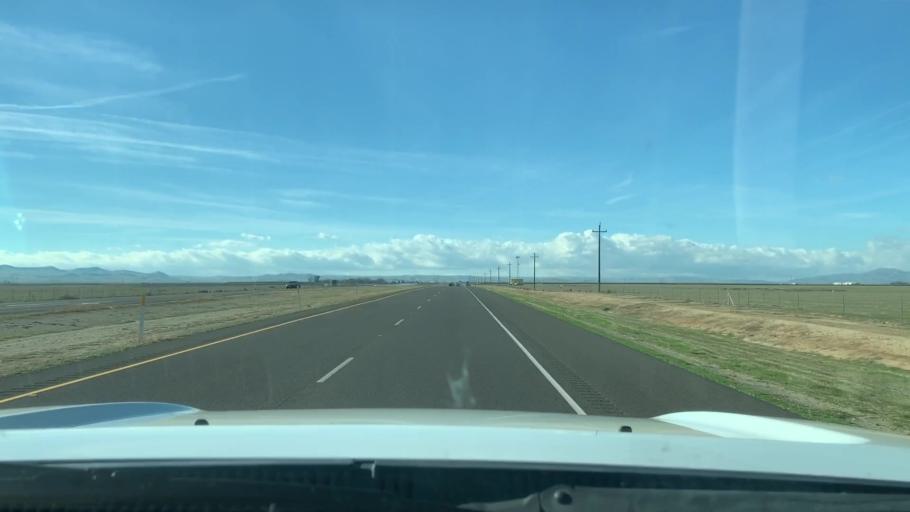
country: US
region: California
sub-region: Kern County
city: Lost Hills
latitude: 35.6155
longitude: -119.8358
